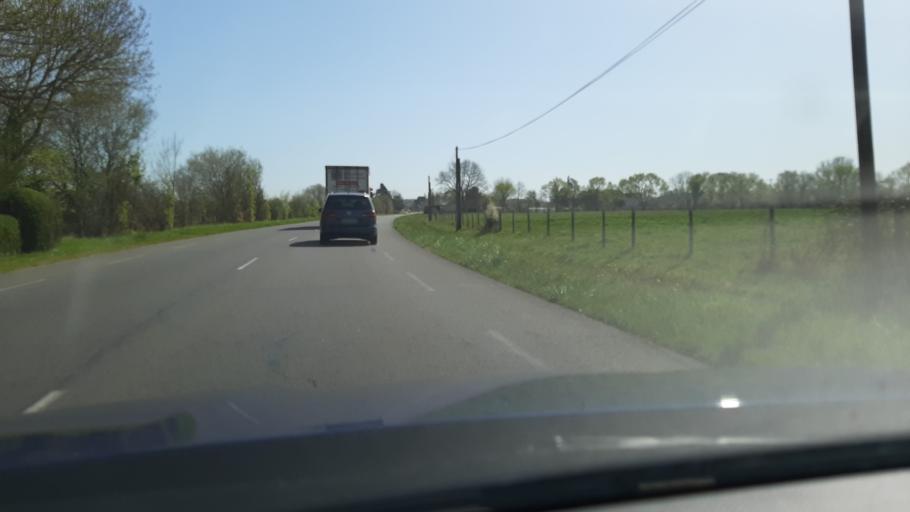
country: FR
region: Pays de la Loire
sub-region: Departement de Maine-et-Loire
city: Ecouflant
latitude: 47.5192
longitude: -0.4864
